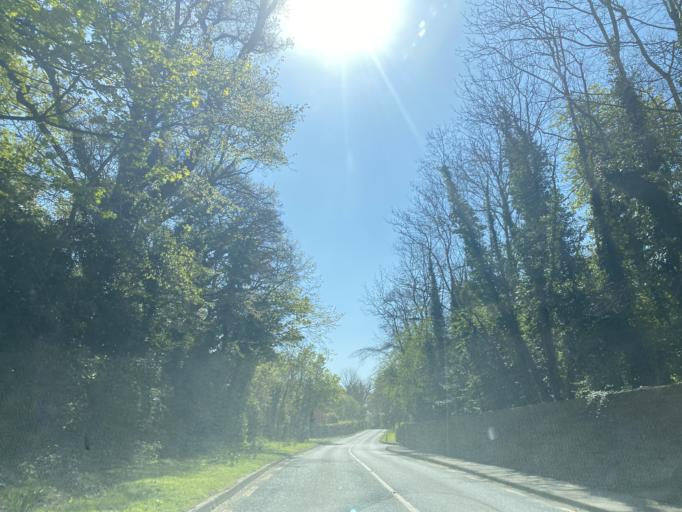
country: IE
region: Leinster
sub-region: Kildare
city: Kill
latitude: 53.3044
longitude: -6.6143
